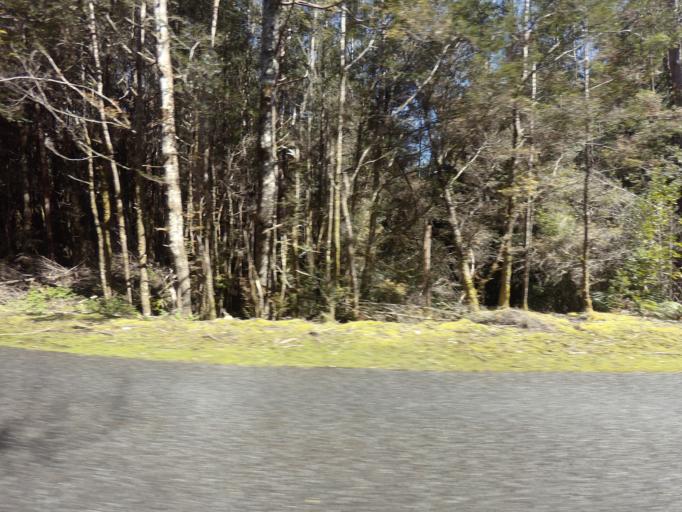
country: AU
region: Tasmania
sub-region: Derwent Valley
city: New Norfolk
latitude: -42.7379
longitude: 146.4222
